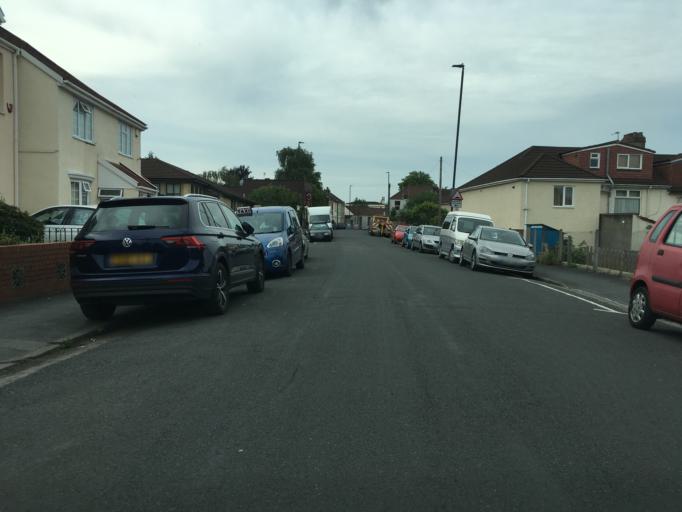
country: GB
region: England
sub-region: Bristol
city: Bristol
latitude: 51.4637
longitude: -2.5575
